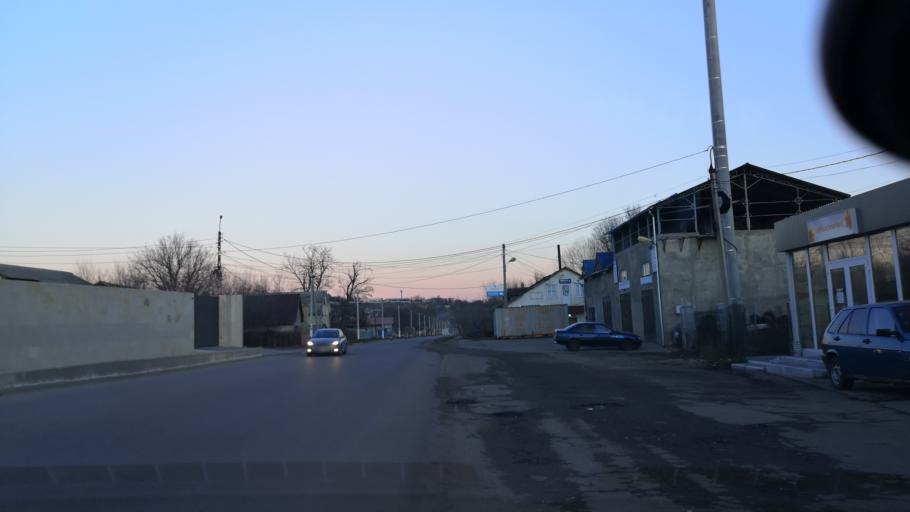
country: MD
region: Anenii Noi
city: Anenii Noi
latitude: 46.8908
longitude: 29.2933
